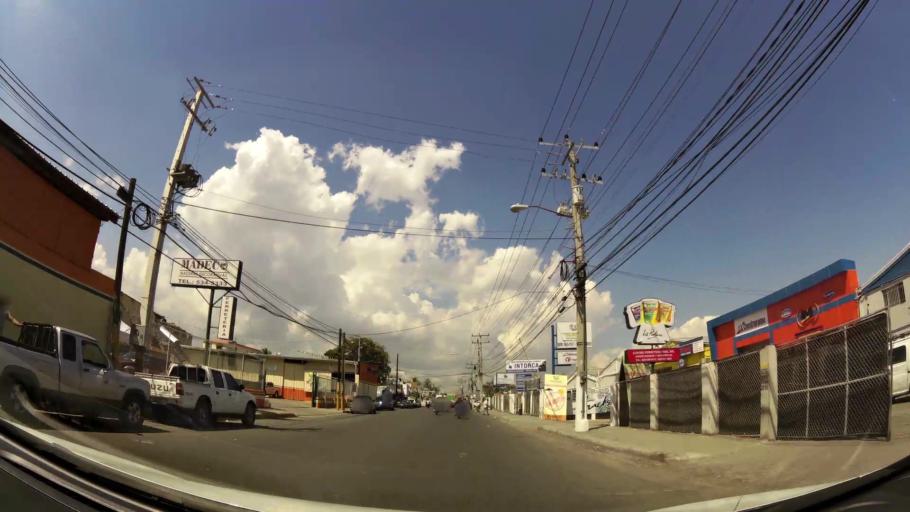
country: DO
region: Nacional
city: Bella Vista
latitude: 18.4555
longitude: -69.9777
